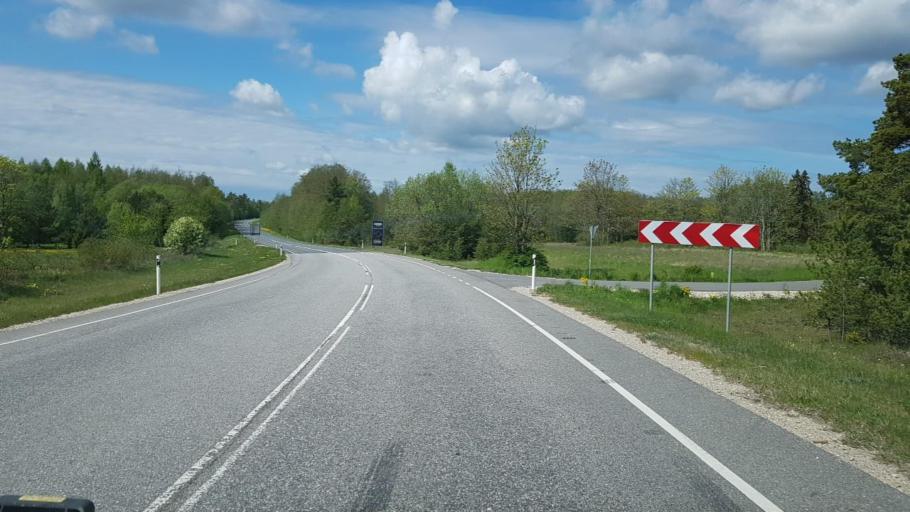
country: EE
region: Hiiumaa
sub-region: Kaerdla linn
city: Kardla
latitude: 58.9896
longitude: 22.7875
